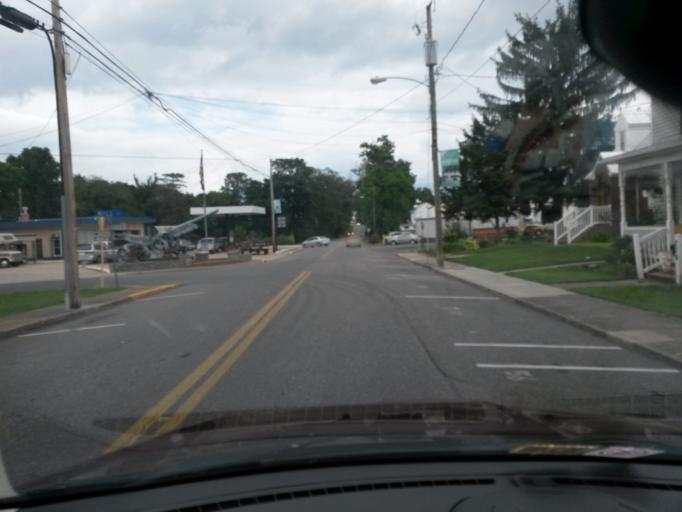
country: US
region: Virginia
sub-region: Rockingham County
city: Dayton
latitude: 38.4156
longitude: -78.9379
